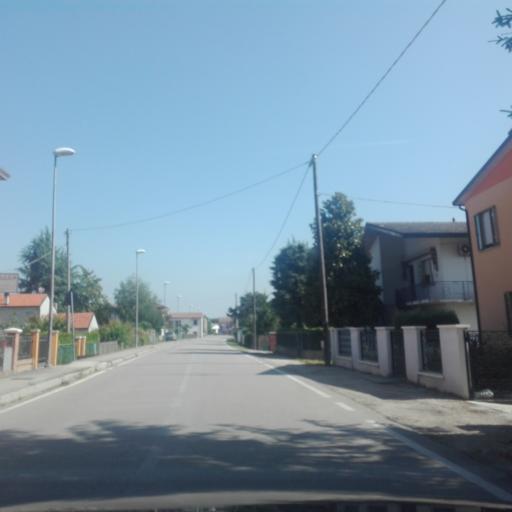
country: IT
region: Veneto
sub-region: Provincia di Rovigo
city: Gavello
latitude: 45.0242
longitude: 11.9152
